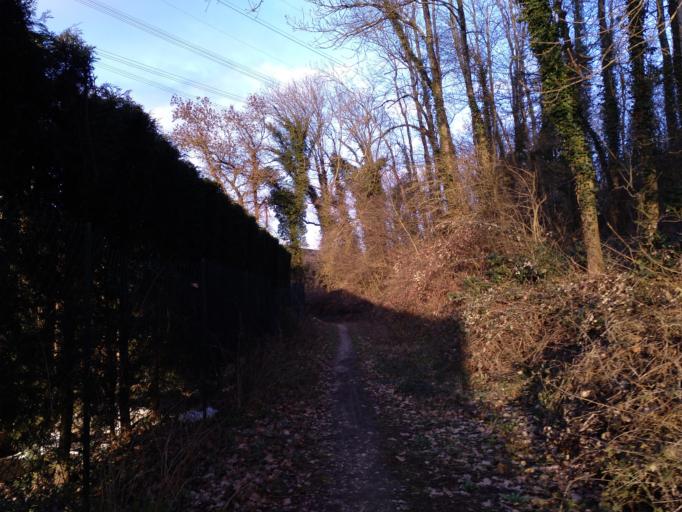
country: FR
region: Rhone-Alpes
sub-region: Departement du Rhone
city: Toussieu
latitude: 45.6657
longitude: 4.9710
